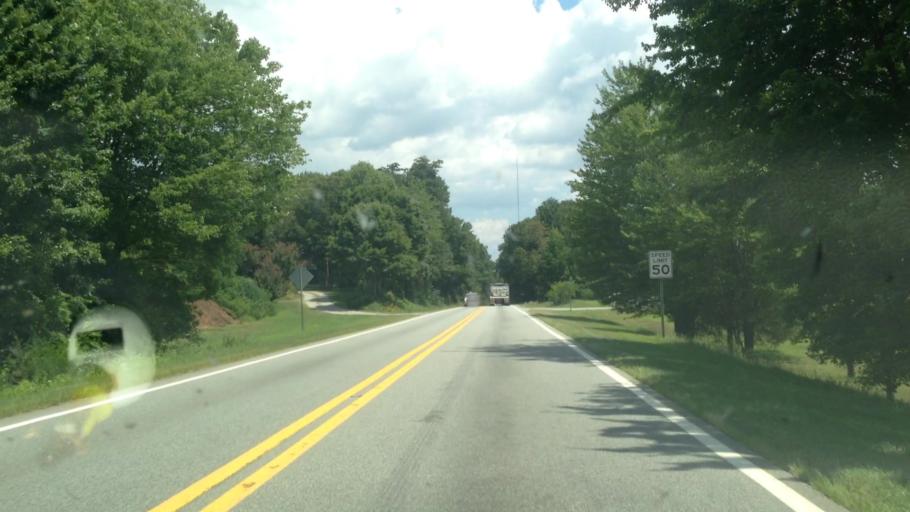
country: US
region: North Carolina
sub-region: Guilford County
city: Stokesdale
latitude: 36.2587
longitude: -79.9583
